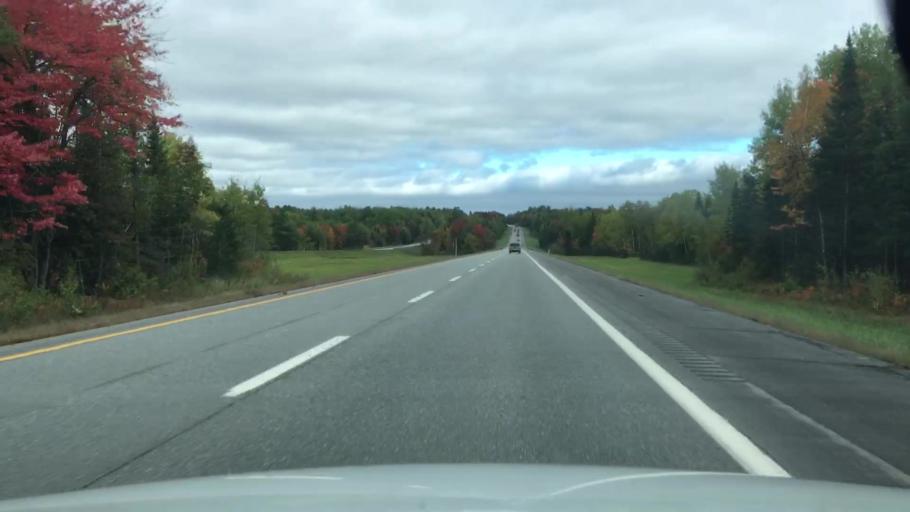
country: US
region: Maine
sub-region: Penobscot County
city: Carmel
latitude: 44.7762
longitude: -69.0489
